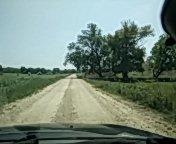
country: HU
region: Fejer
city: Bicske
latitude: 47.4701
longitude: 18.5860
